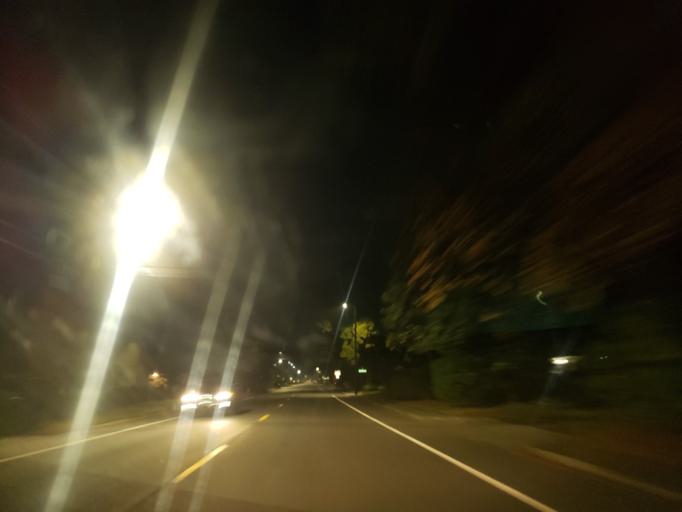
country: US
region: Georgia
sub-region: Chatham County
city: Savannah
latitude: 32.0399
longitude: -81.1015
